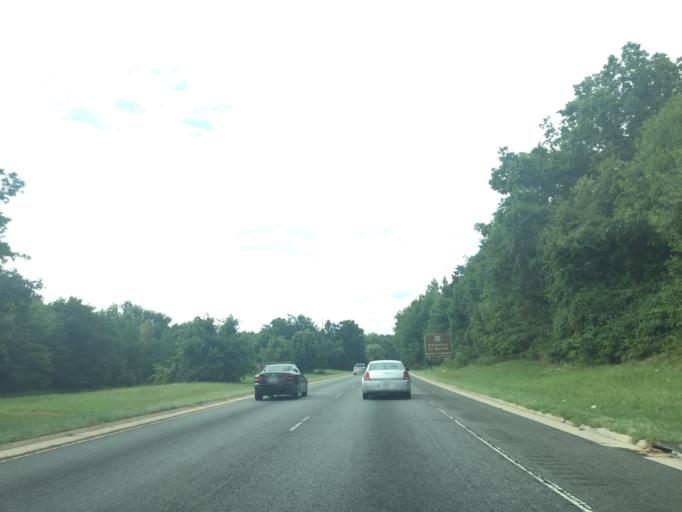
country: US
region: Maryland
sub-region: Anne Arundel County
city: Jessup
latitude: 39.1335
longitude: -76.7592
